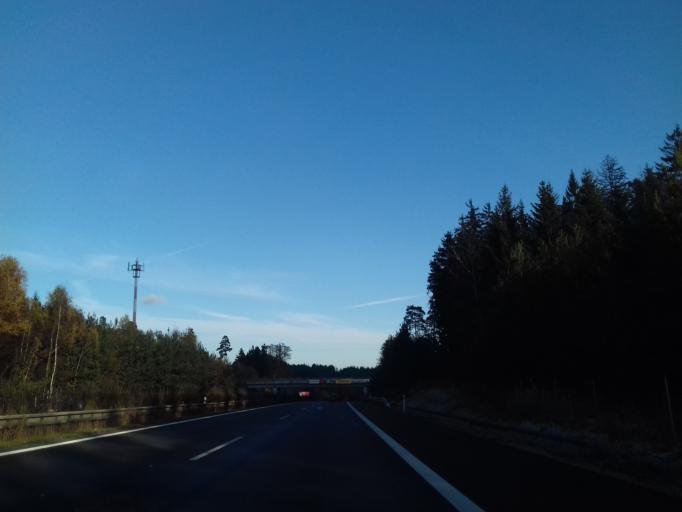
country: CZ
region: Plzensky
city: Holoubkov
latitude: 49.7807
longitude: 13.6859
